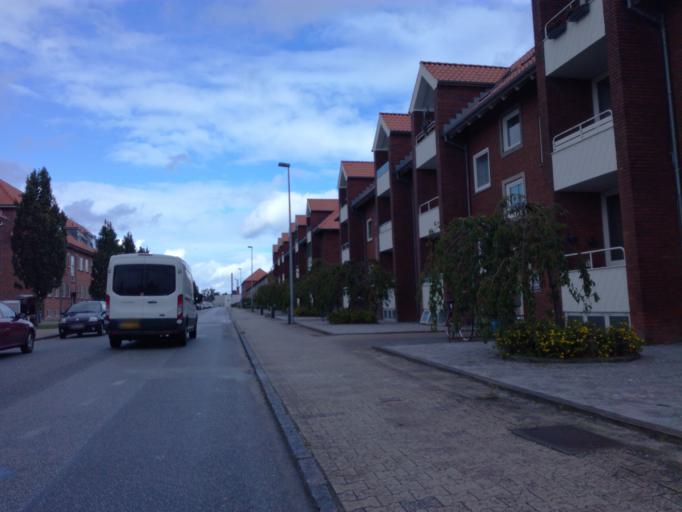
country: DK
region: South Denmark
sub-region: Fredericia Kommune
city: Fredericia
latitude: 55.5748
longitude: 9.7439
